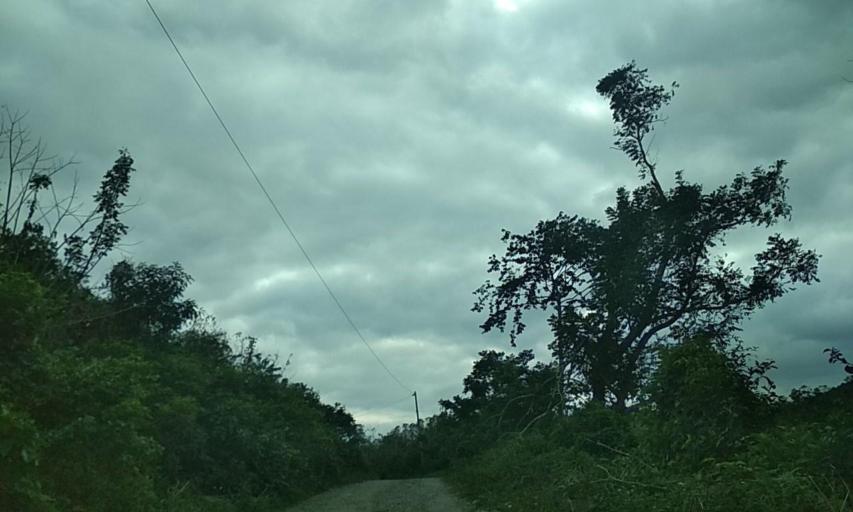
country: MX
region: Veracruz
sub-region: Papantla
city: Polutla
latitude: 20.5115
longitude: -97.2974
